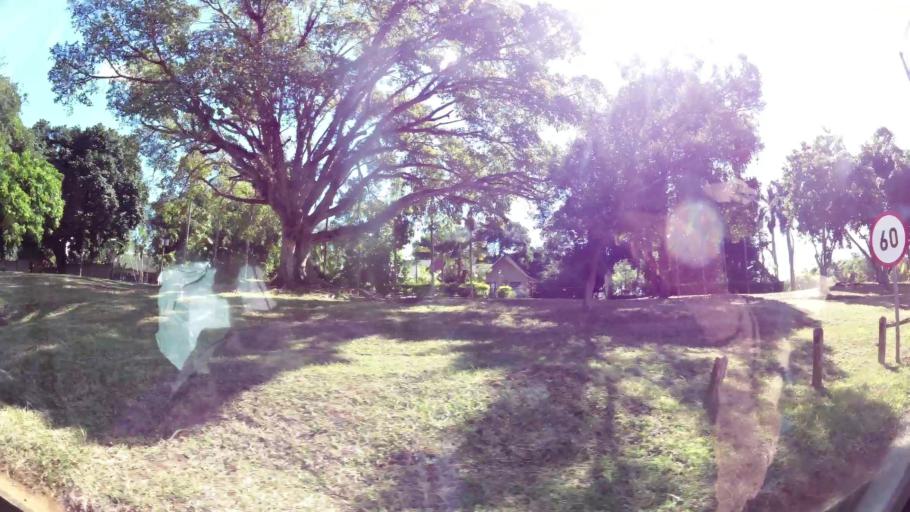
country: ZA
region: Limpopo
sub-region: Mopani District Municipality
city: Tzaneen
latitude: -23.8408
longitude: 30.1506
